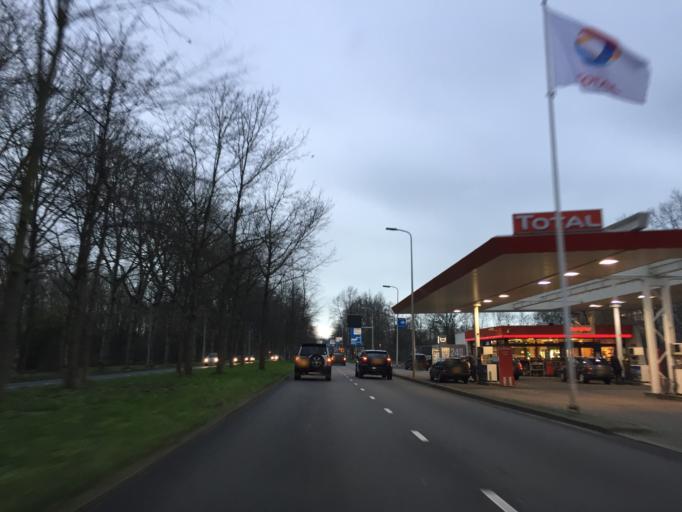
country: NL
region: South Holland
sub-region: Gemeente Westland
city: Kwintsheul
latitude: 52.0407
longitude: 4.2447
